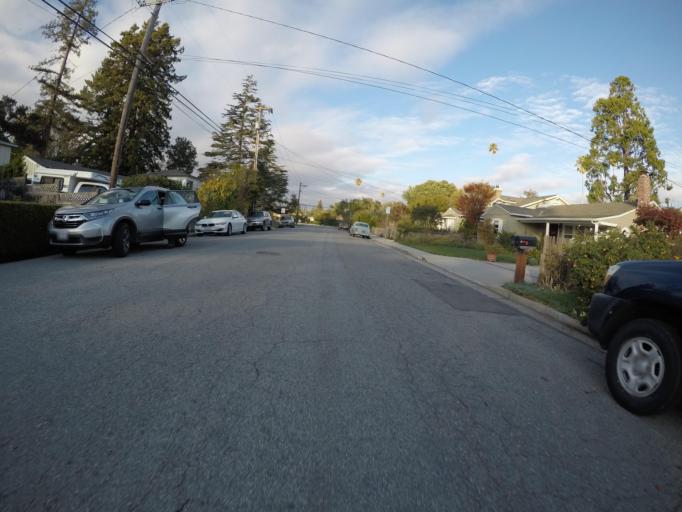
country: US
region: California
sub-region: Santa Cruz County
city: Santa Cruz
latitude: 36.9770
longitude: -122.0437
